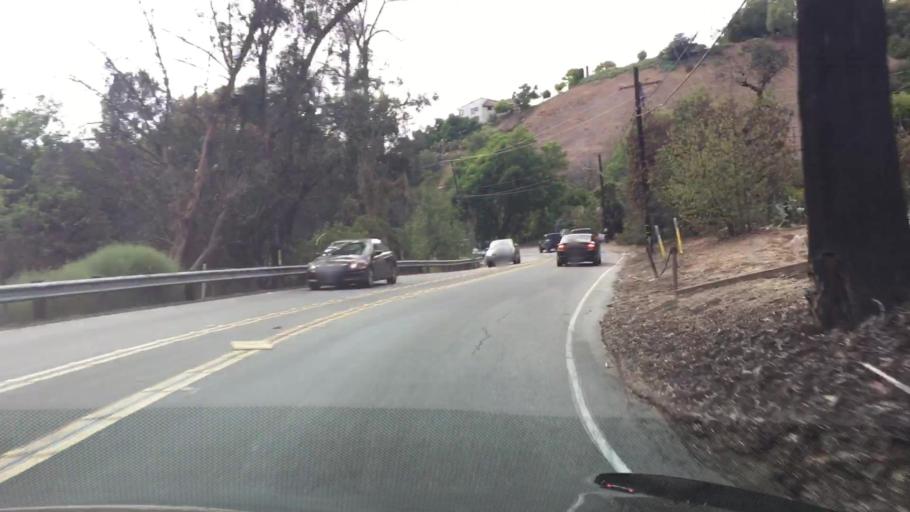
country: US
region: California
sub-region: Los Angeles County
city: La Habra Heights
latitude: 33.9653
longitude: -117.9578
